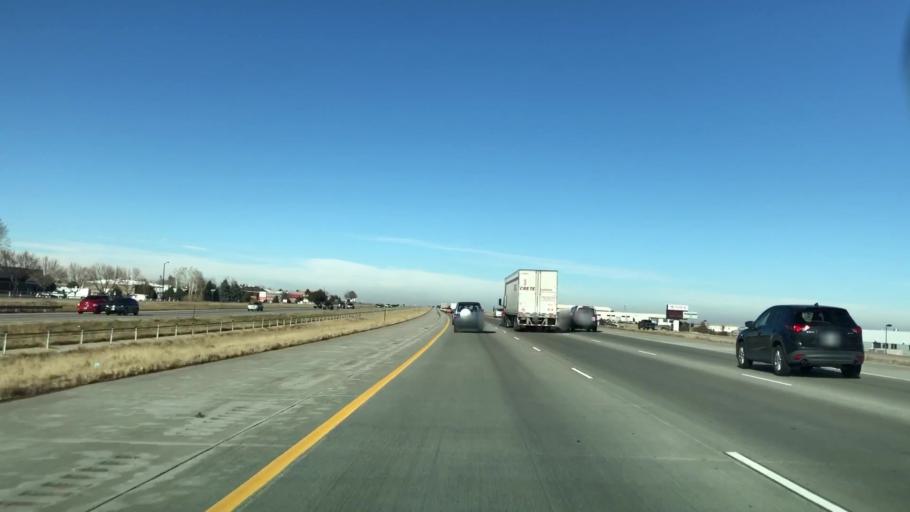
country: US
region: Colorado
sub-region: Weld County
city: Firestone
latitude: 40.1166
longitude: -104.9798
